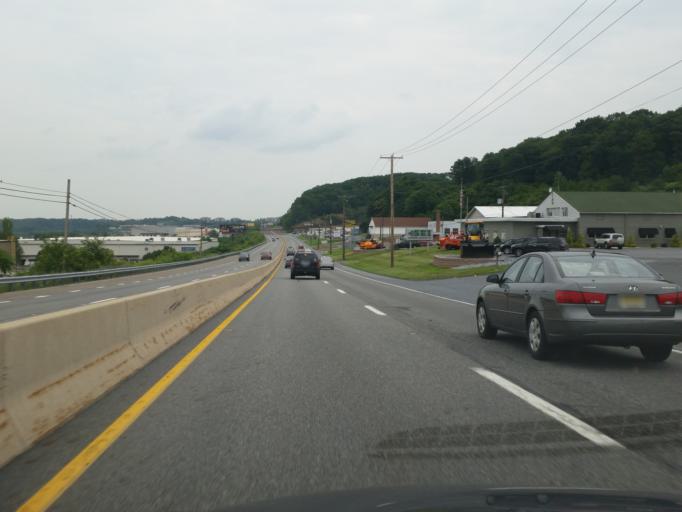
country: US
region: Pennsylvania
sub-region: Dauphin County
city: Rutherford
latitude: 40.2606
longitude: -76.7674
